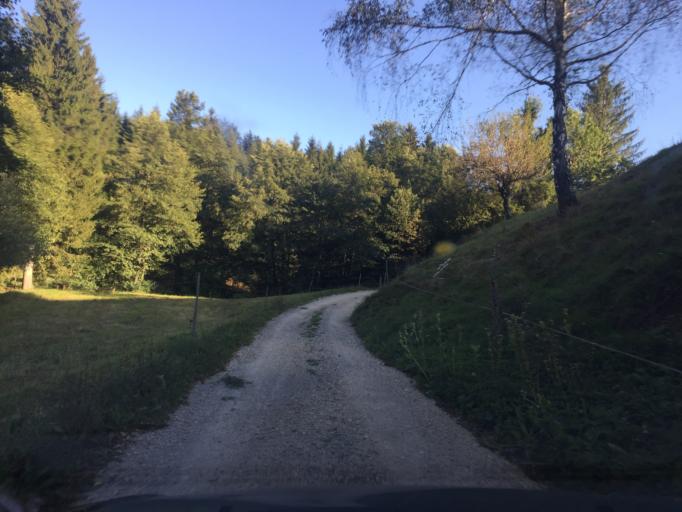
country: SI
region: Postojna
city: Postojna
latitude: 45.8100
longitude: 14.1329
